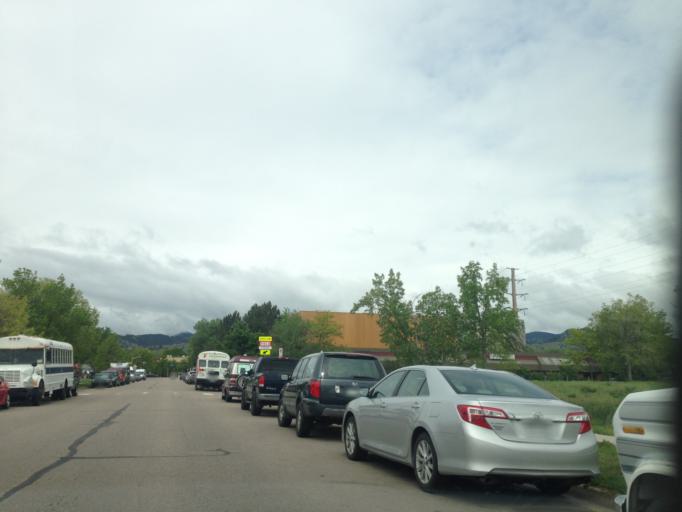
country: US
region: Colorado
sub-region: Boulder County
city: Boulder
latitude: 40.0256
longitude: -105.2552
